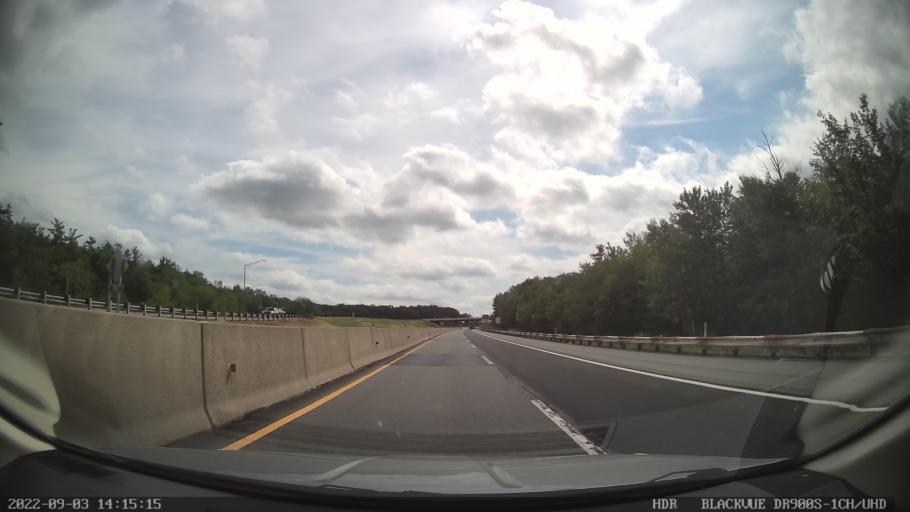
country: US
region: Pennsylvania
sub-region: Carbon County
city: Towamensing Trails
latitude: 40.9746
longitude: -75.6284
